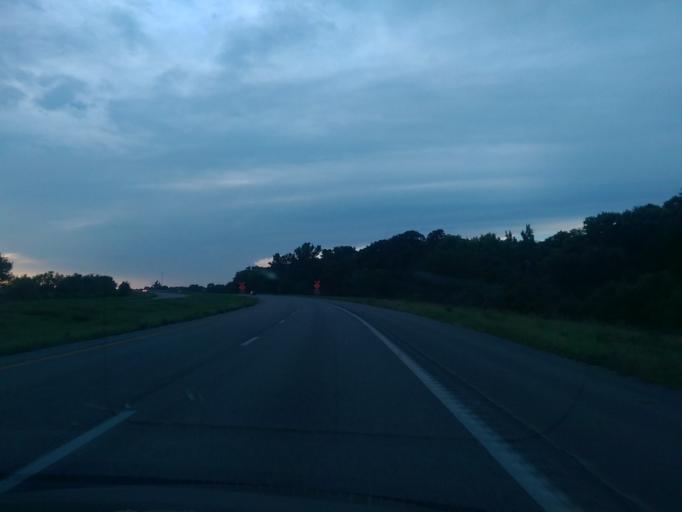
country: US
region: Missouri
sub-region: Atchison County
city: Rock Port
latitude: 40.3426
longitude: -95.5036
